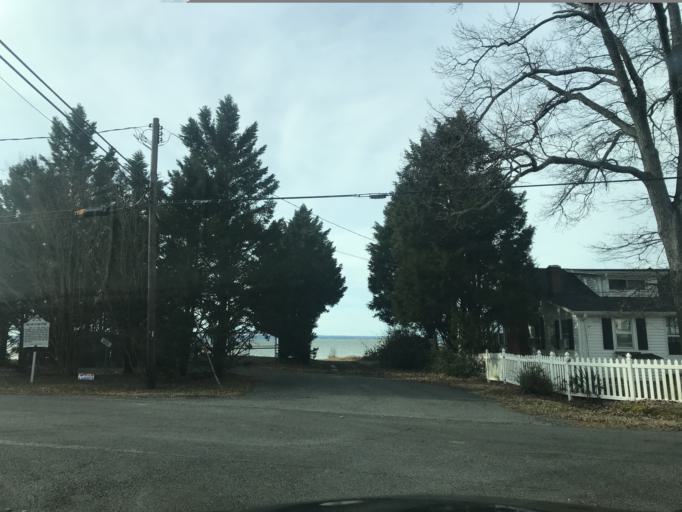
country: US
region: Maryland
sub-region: Charles County
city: Cobb Island
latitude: 38.2610
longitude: -76.8513
